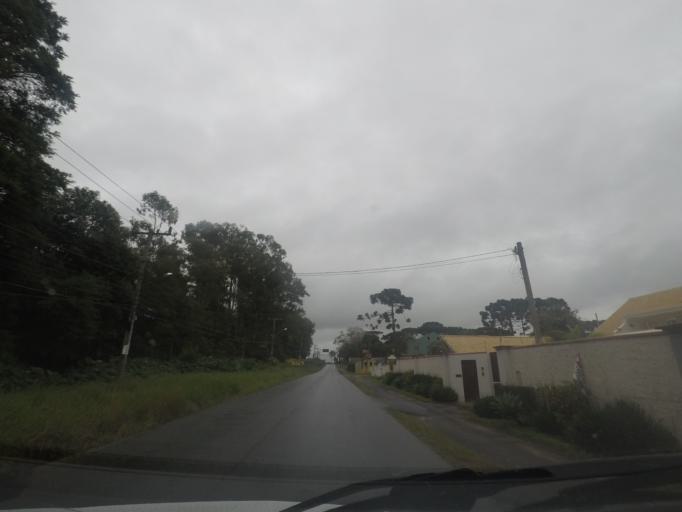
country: BR
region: Parana
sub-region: Quatro Barras
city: Quatro Barras
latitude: -25.3857
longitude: -49.1375
